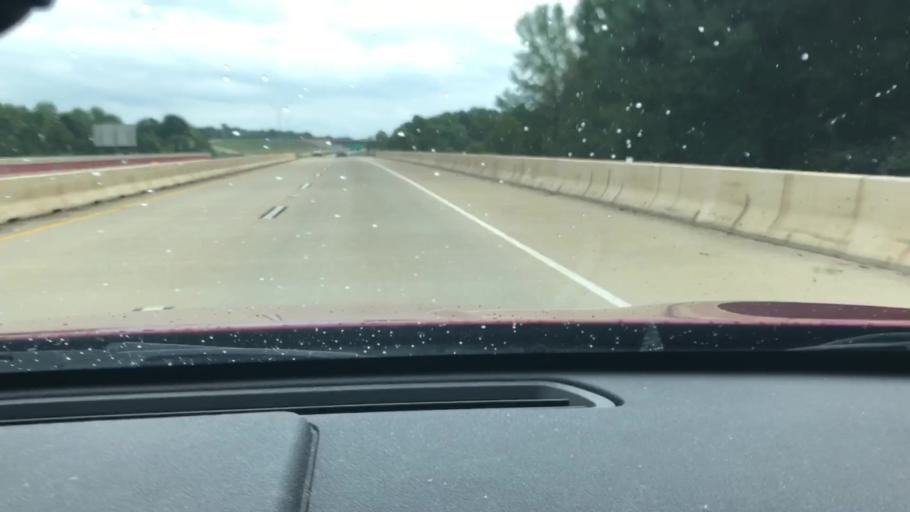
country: US
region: Texas
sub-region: Bowie County
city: Texarkana
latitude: 33.3848
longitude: -94.0524
